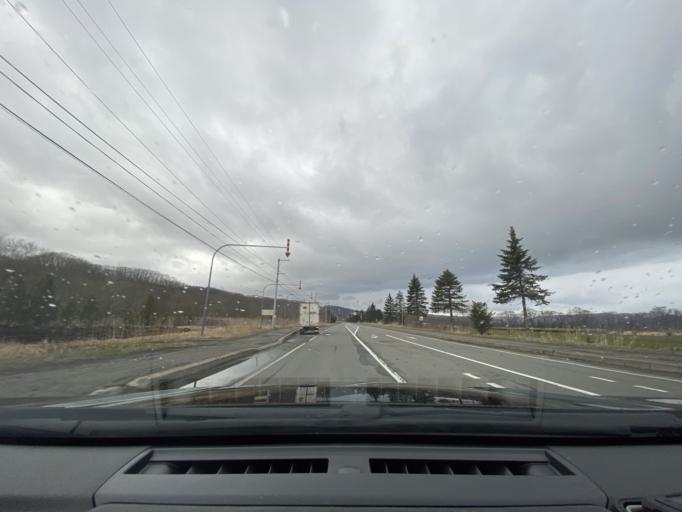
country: JP
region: Hokkaido
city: Otofuke
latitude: 43.2121
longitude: 143.5604
